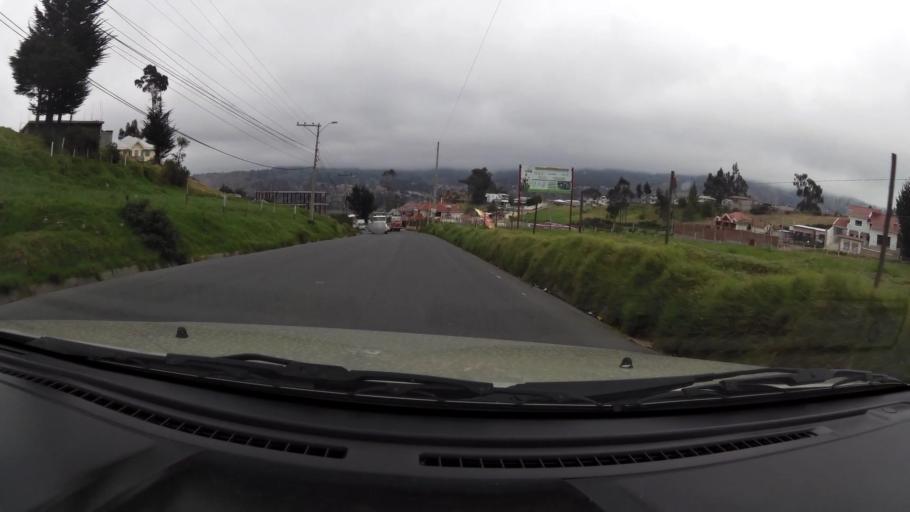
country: EC
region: Canar
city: Canar
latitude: -2.5372
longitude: -78.9321
